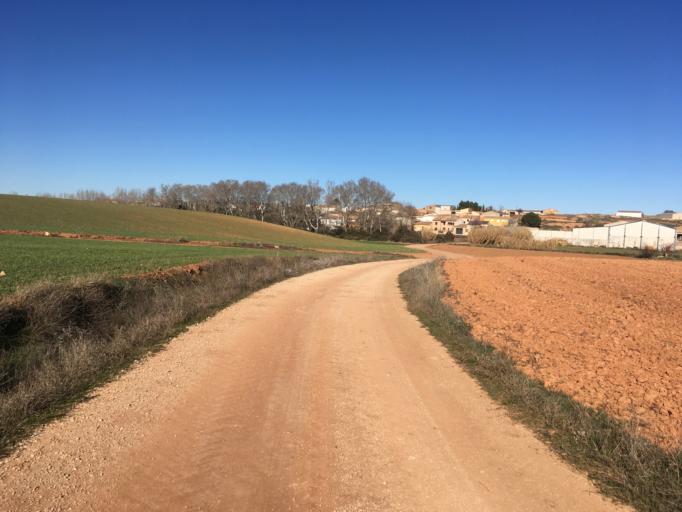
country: ES
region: Castille-La Mancha
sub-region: Provincia de Cuenca
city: Atalaya del Canavate
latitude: 39.5448
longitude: -2.2468
